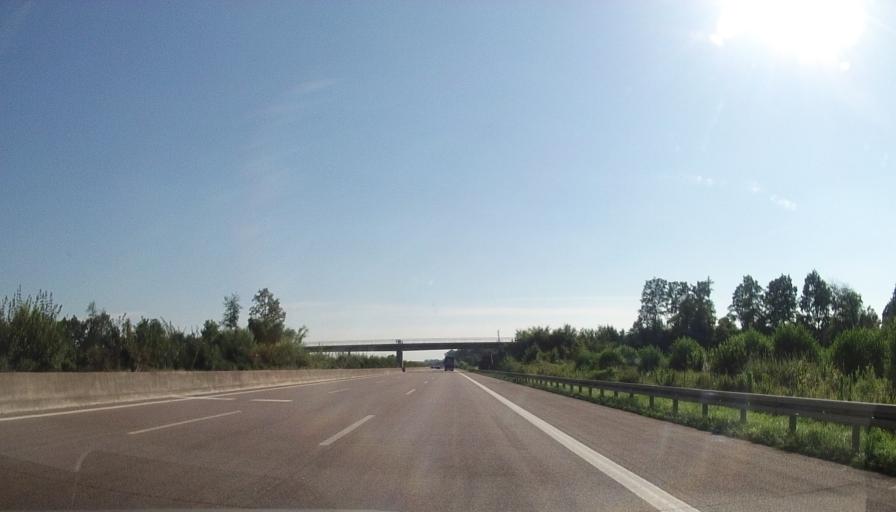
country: DE
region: Baden-Wuerttemberg
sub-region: Freiburg Region
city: Appenweier
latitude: 48.5701
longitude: 7.9613
